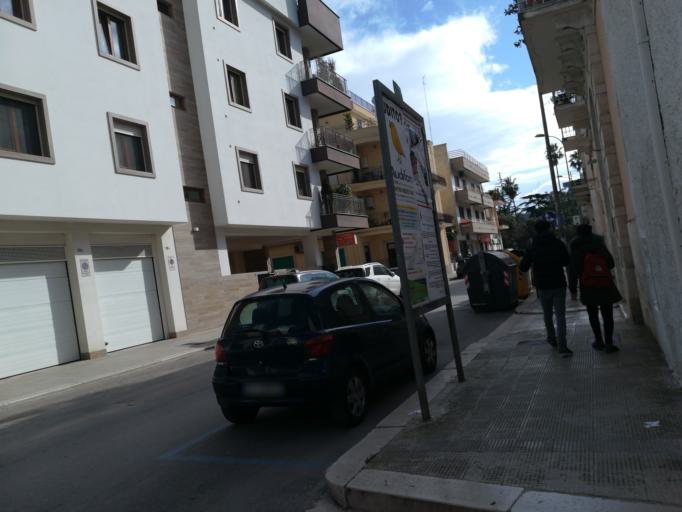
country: IT
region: Apulia
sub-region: Provincia di Bari
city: Bitonto
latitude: 41.1124
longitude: 16.6942
